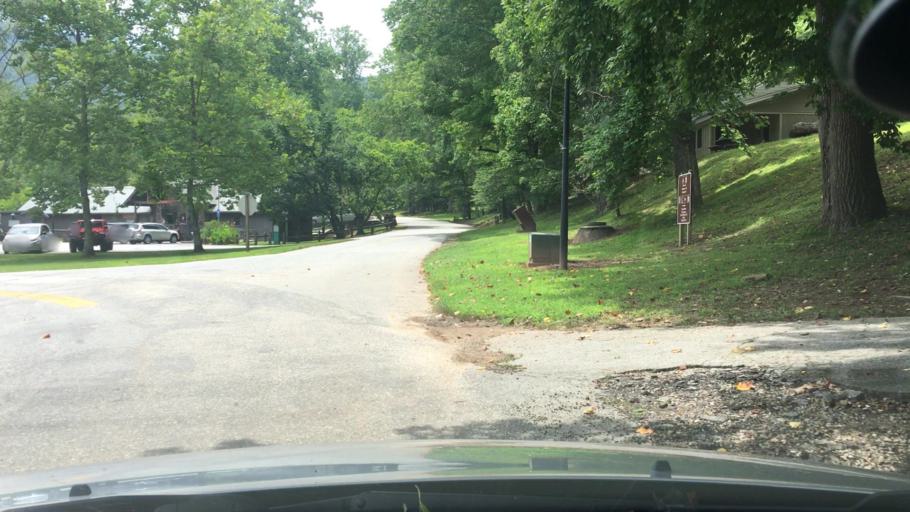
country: US
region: Georgia
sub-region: Union County
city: Blairsville
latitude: 34.7664
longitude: -83.9236
